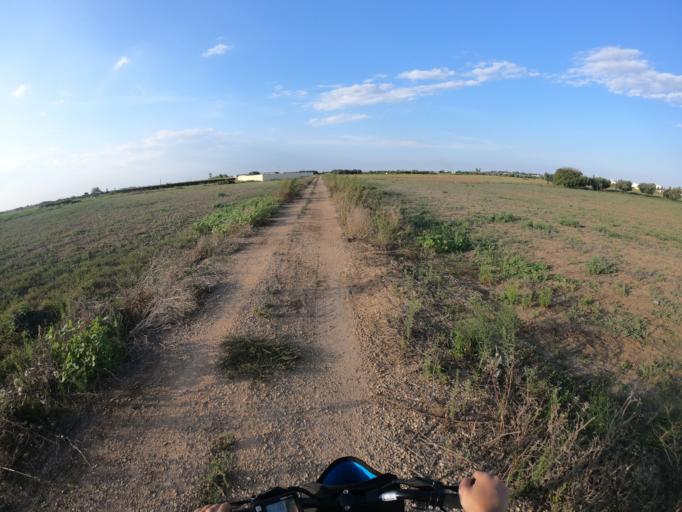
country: IT
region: Apulia
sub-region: Provincia di Lecce
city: Nardo
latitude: 40.1719
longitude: 18.0120
